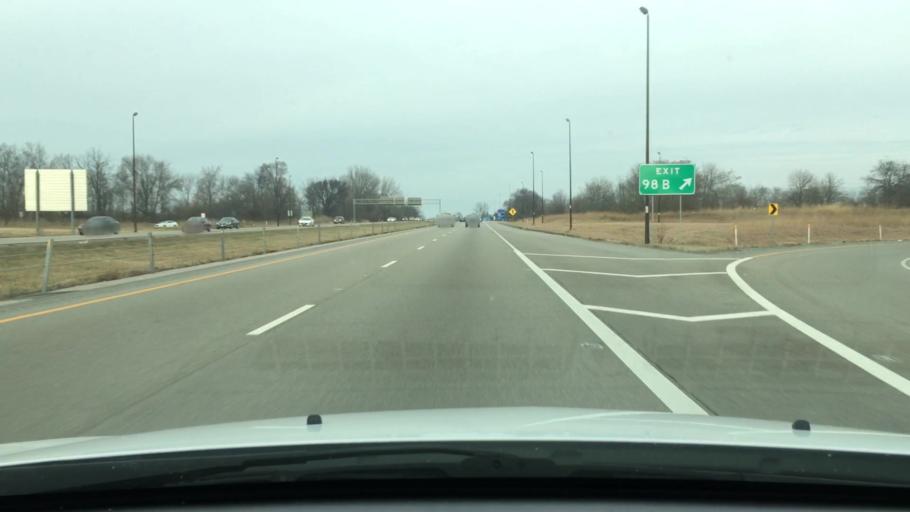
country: US
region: Illinois
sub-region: Sangamon County
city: Grandview
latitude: 39.8028
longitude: -89.5948
